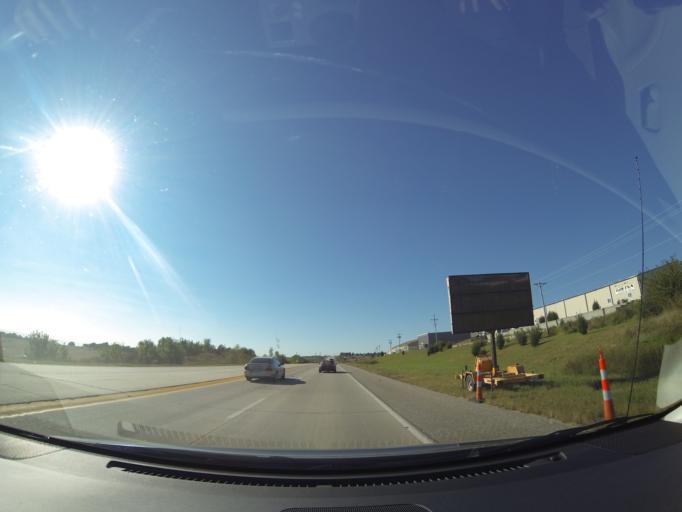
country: US
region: Nebraska
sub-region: Sarpy County
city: Gretna
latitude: 41.1097
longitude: -96.2535
